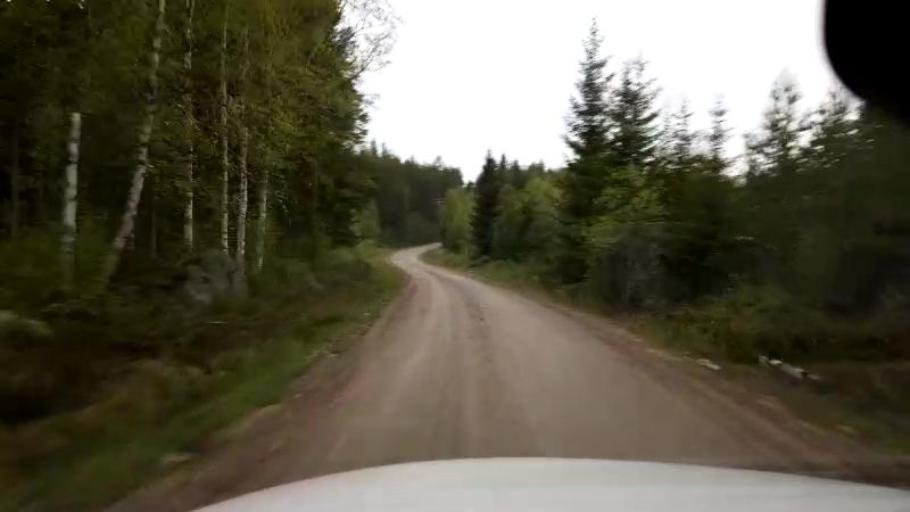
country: SE
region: Gaevleborg
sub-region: Ljusdals Kommun
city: Jaervsoe
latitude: 61.7678
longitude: 16.1876
